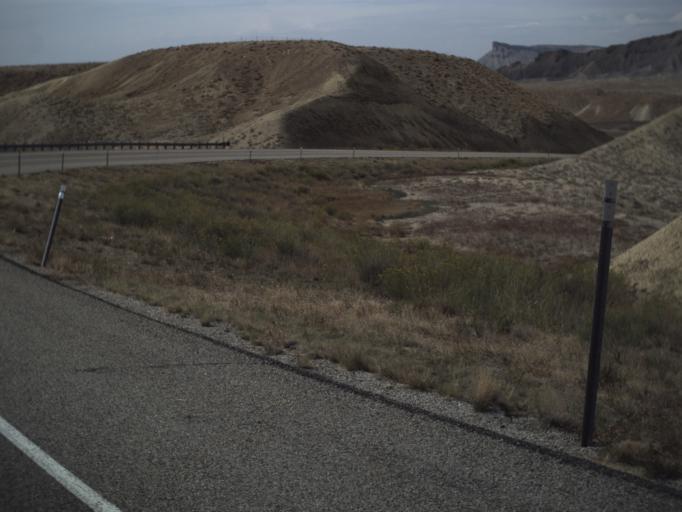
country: US
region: Utah
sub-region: Grand County
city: Moab
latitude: 38.9366
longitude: -109.8296
